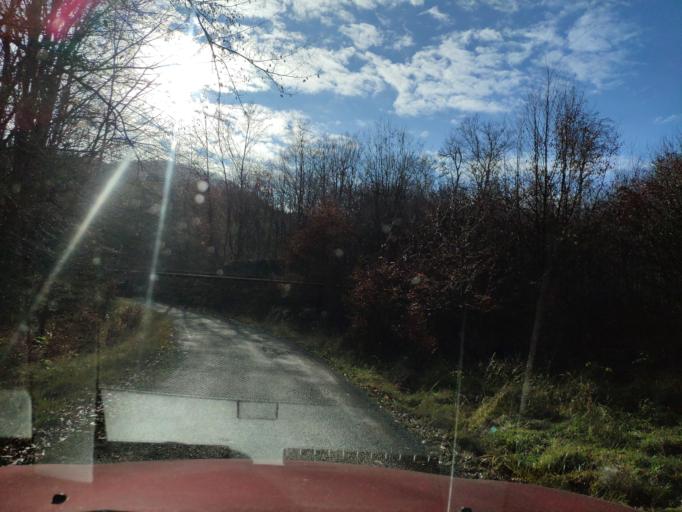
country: HU
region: Borsod-Abauj-Zemplen
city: Gonc
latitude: 48.5980
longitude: 21.4465
